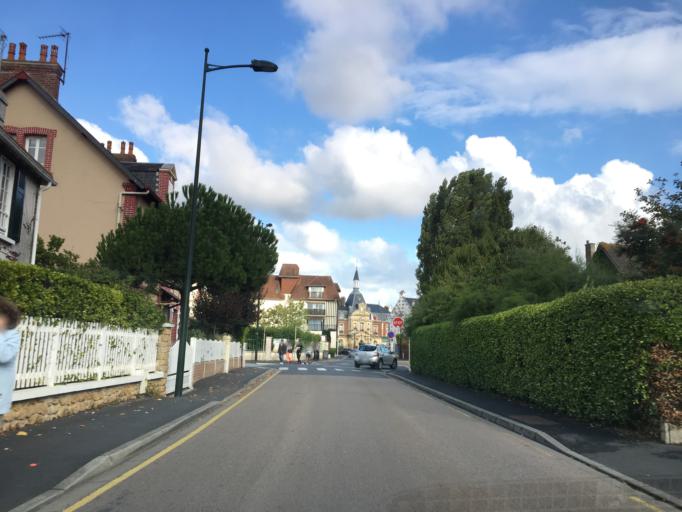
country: FR
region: Lower Normandy
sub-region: Departement du Calvados
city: Cabourg
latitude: 49.2887
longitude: -0.1180
